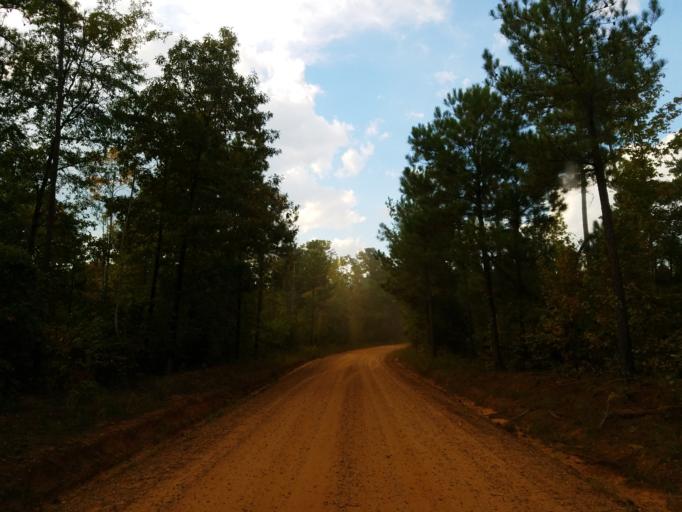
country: US
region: Georgia
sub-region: Monroe County
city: Forsyth
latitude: 33.1157
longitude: -84.0214
